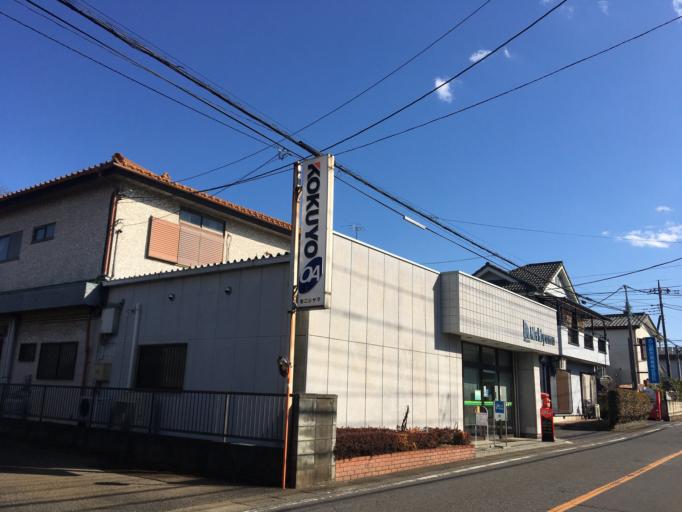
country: JP
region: Saitama
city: Oi
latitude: 35.8589
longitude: 139.5117
